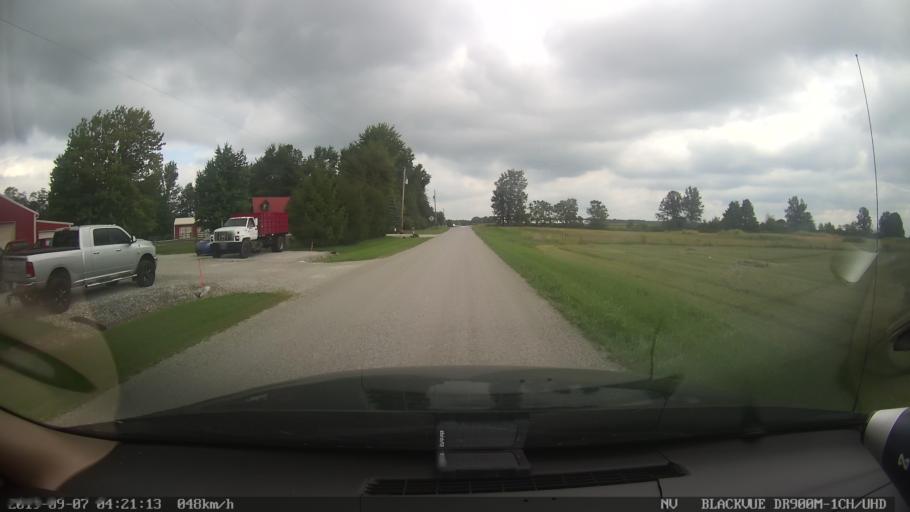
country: US
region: Ohio
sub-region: Knox County
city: Centerburg
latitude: 40.2647
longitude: -82.6728
